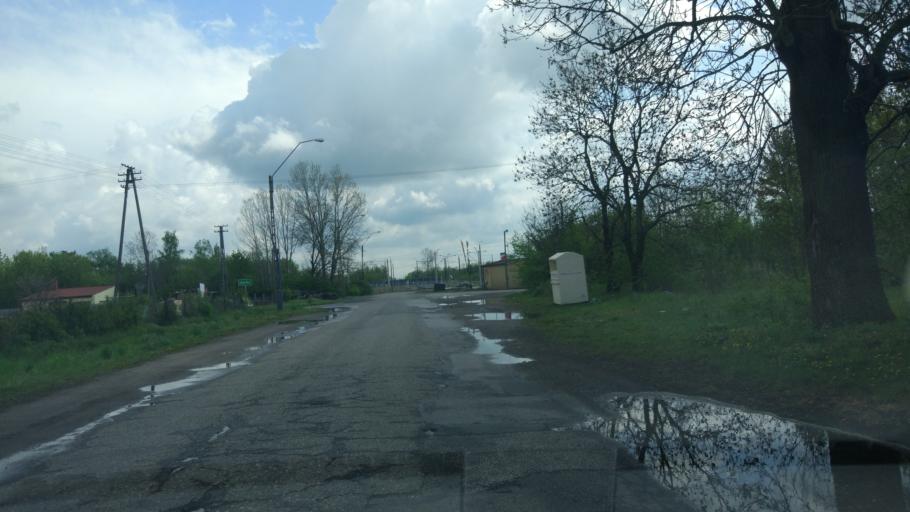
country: PL
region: Lodz Voivodeship
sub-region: Powiat kutnowski
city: Kutno
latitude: 52.2257
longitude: 19.4032
